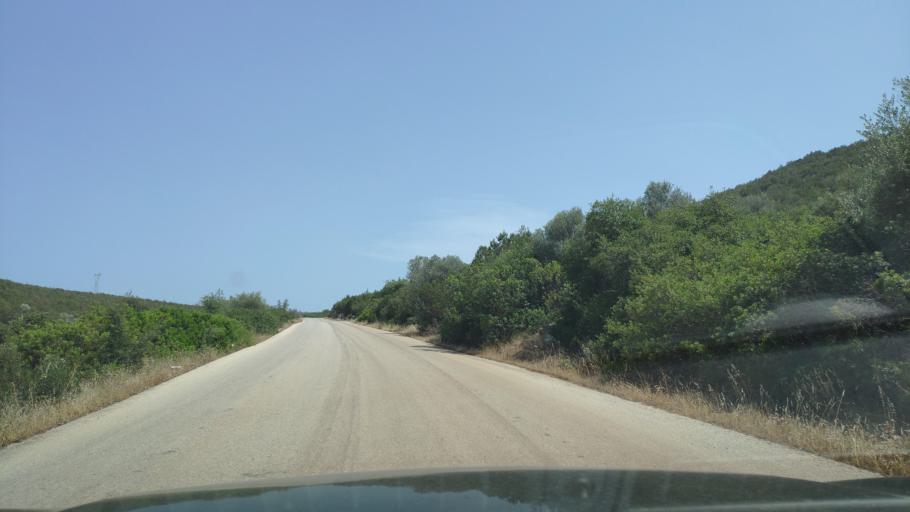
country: GR
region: Peloponnese
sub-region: Nomos Argolidos
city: Didyma
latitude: 37.4475
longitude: 23.1808
